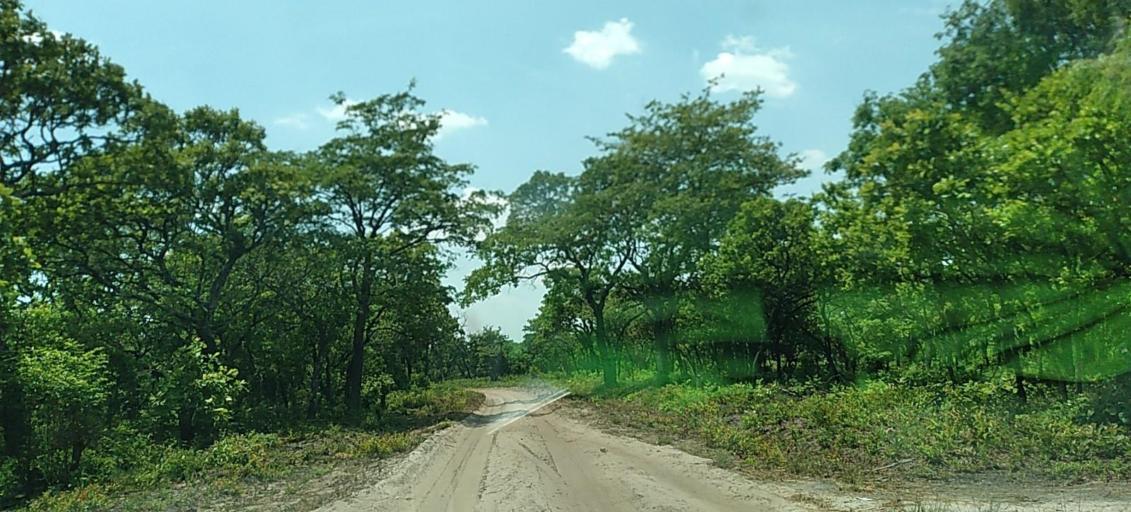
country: CD
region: Katanga
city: Kolwezi
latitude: -11.3045
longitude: 25.2321
